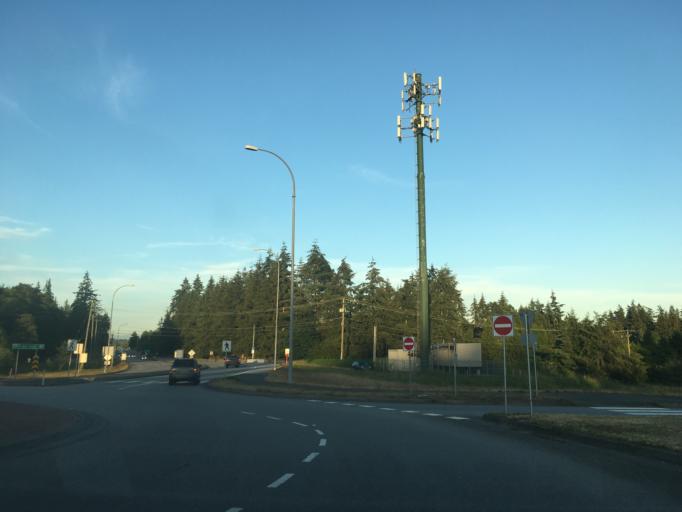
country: US
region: Washington
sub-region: Whatcom County
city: Blaine
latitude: 49.0167
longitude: -122.7584
